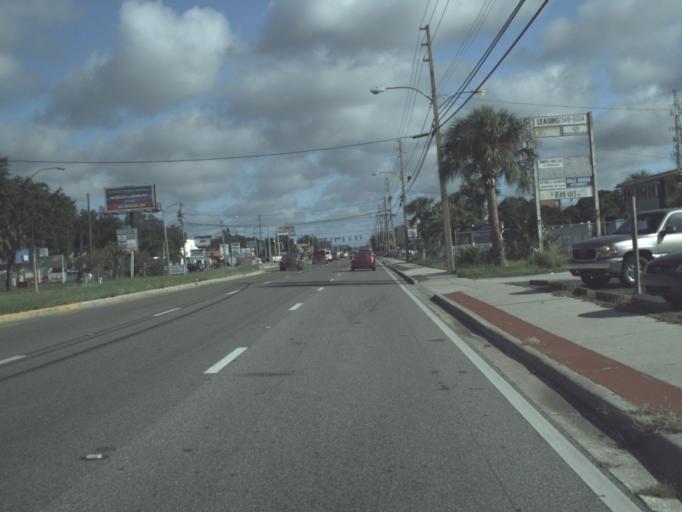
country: US
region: Florida
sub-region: Pinellas County
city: Kenneth City
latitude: 27.8183
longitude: -82.7284
